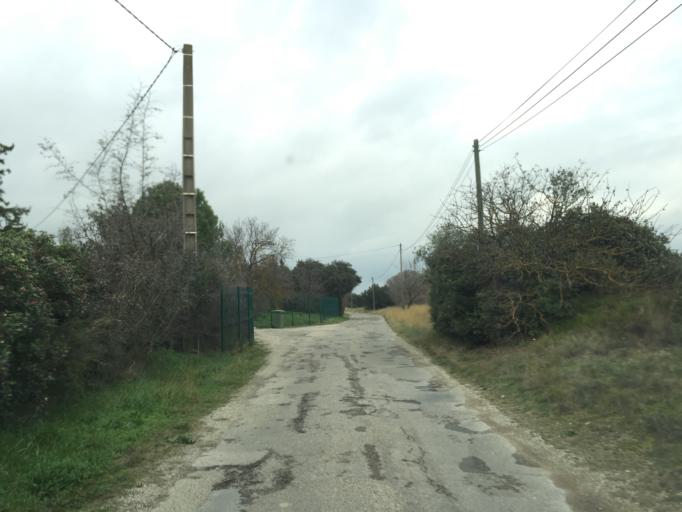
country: FR
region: Provence-Alpes-Cote d'Azur
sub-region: Departement du Vaucluse
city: Sorgues
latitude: 44.0229
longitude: 4.8739
